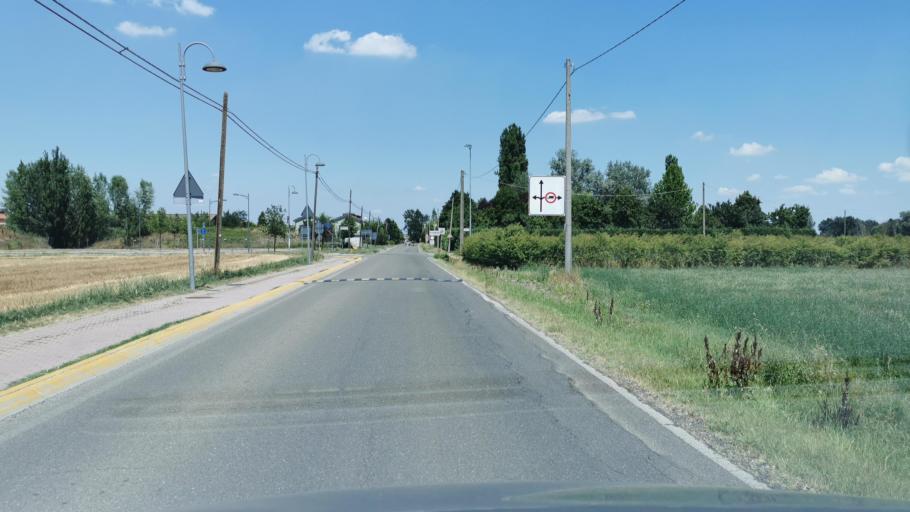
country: IT
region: Emilia-Romagna
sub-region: Provincia di Modena
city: Fossoli
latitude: 44.8145
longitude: 10.8936
